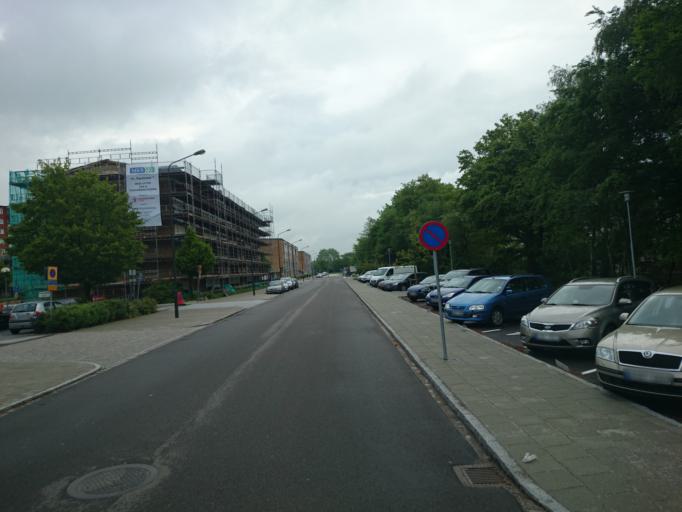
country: SE
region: Skane
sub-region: Burlovs Kommun
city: Arloev
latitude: 55.6156
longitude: 13.0553
